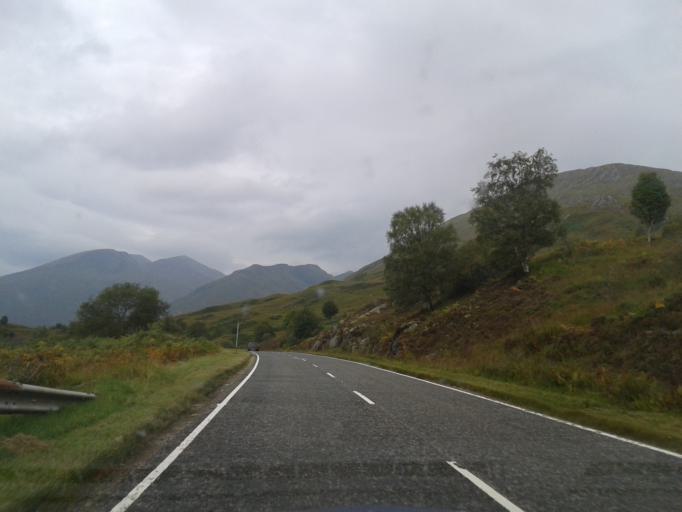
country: GB
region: Scotland
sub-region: Highland
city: Spean Bridge
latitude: 57.1525
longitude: -5.1263
